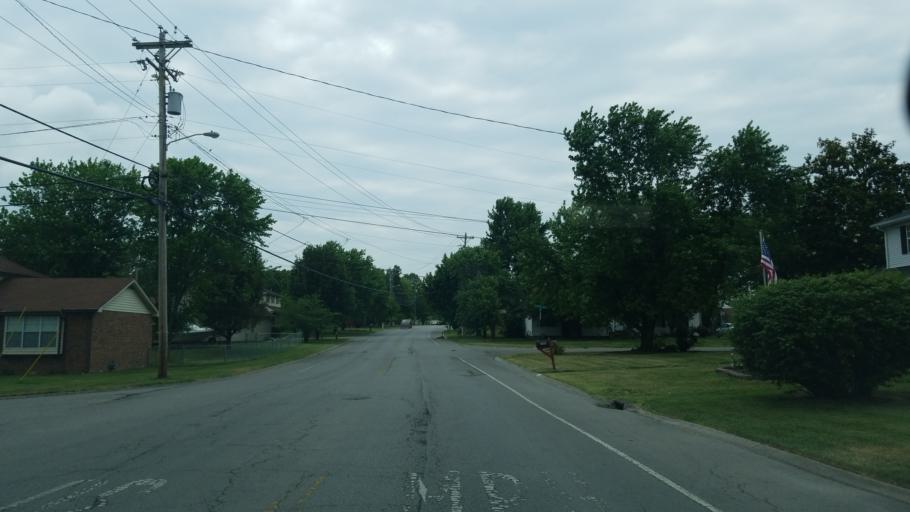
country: US
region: Tennessee
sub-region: Rutherford County
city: La Vergne
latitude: 36.0759
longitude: -86.6028
